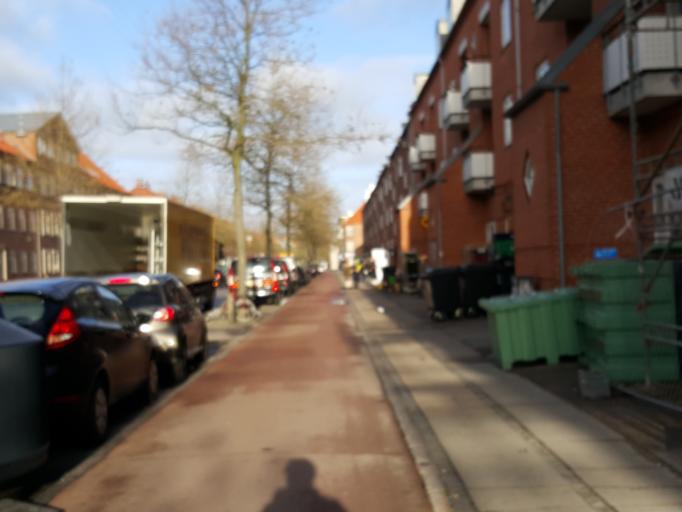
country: DK
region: Capital Region
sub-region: Tarnby Kommune
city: Tarnby
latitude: 55.6471
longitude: 12.6142
